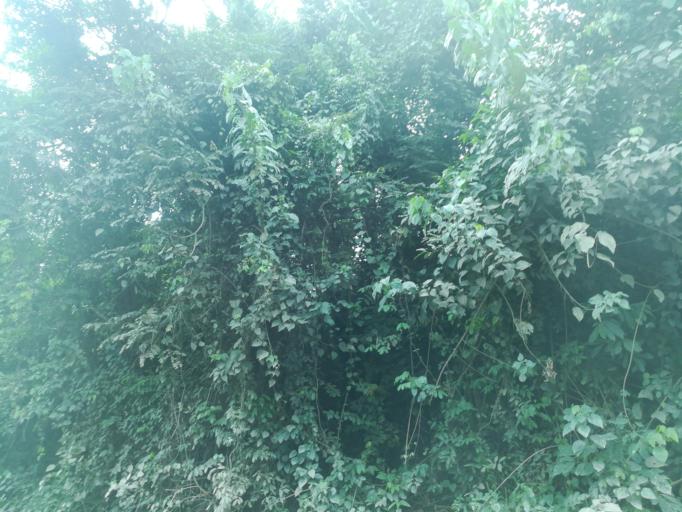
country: NG
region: Lagos
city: Ejirin
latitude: 6.6425
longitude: 3.8559
